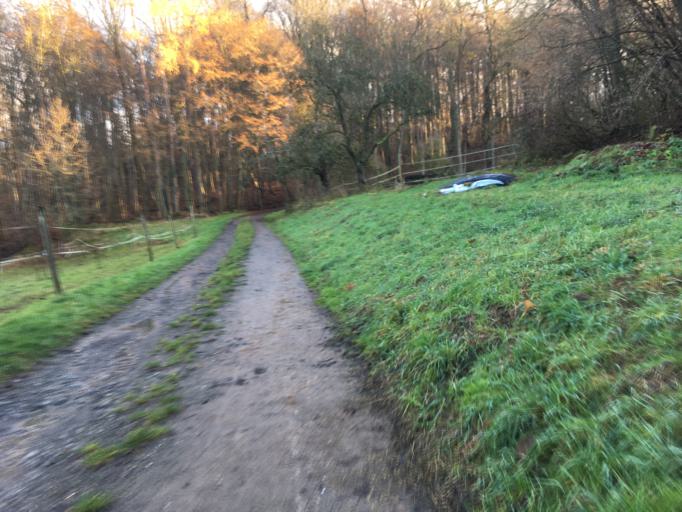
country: DE
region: Baden-Wuerttemberg
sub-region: Regierungsbezirk Stuttgart
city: Talheim
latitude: 49.0743
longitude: 9.1979
